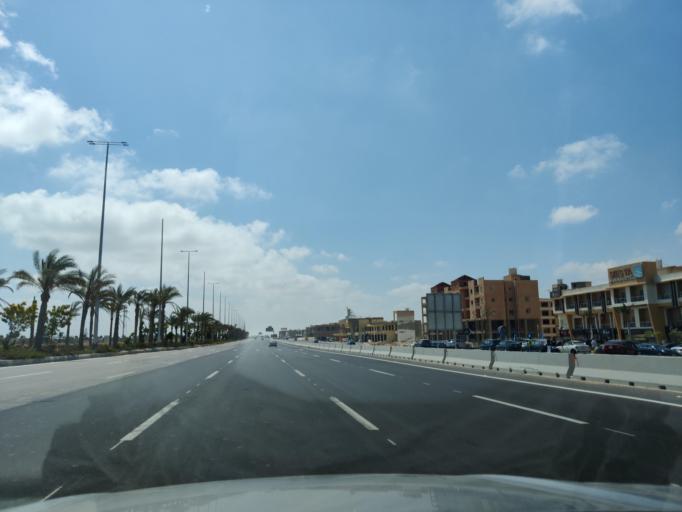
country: EG
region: Muhafazat Matruh
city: Al `Alamayn
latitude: 30.8324
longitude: 28.9654
